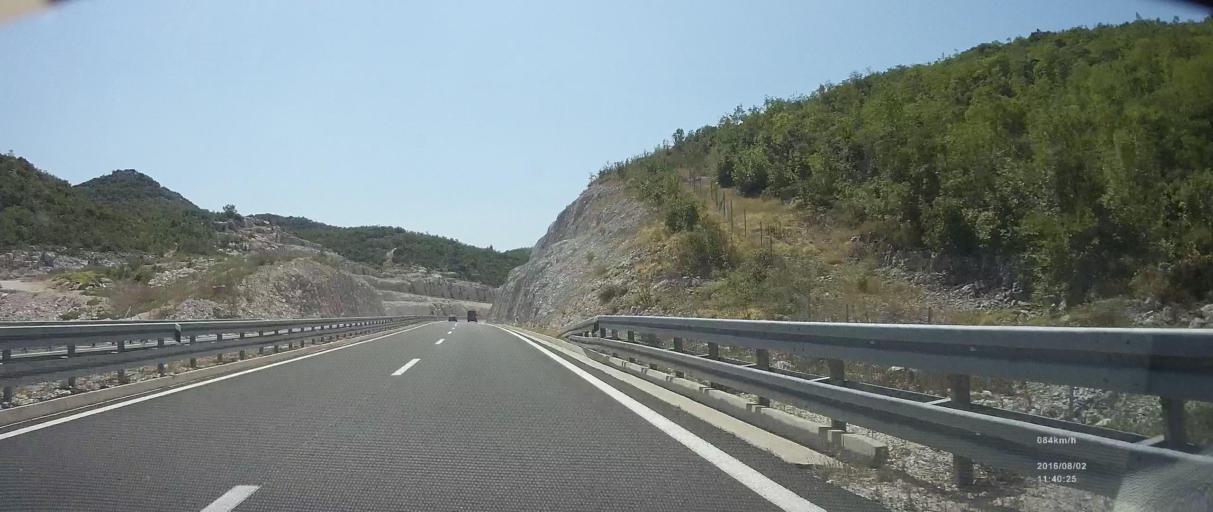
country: HR
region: Dubrovacko-Neretvanska
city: Komin
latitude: 43.0748
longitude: 17.4913
